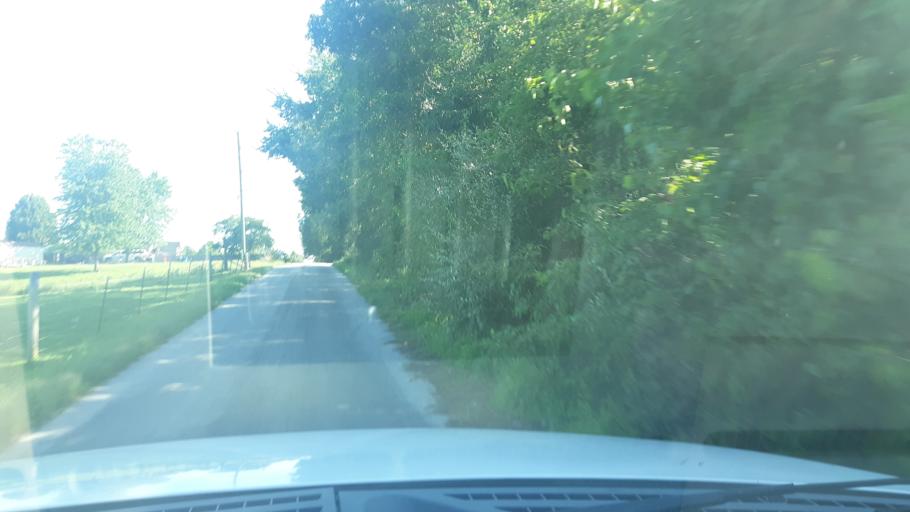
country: US
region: Illinois
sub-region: Saline County
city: Harrisburg
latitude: 37.8604
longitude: -88.5963
